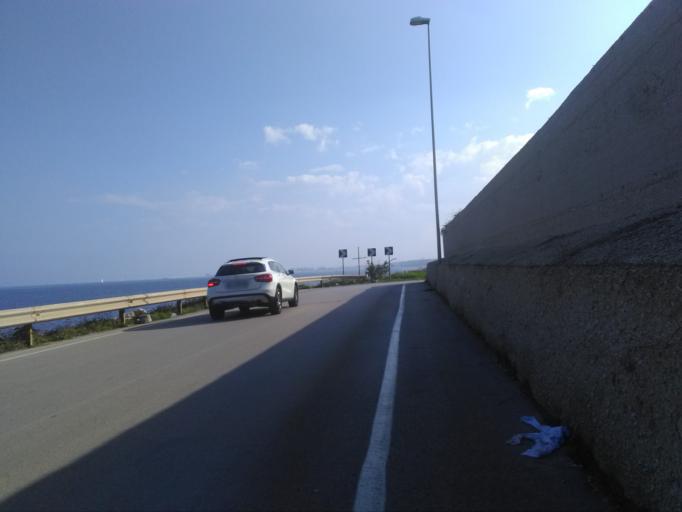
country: IT
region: Apulia
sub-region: Provincia di Bari
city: San Paolo
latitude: 41.1517
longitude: 16.7887
